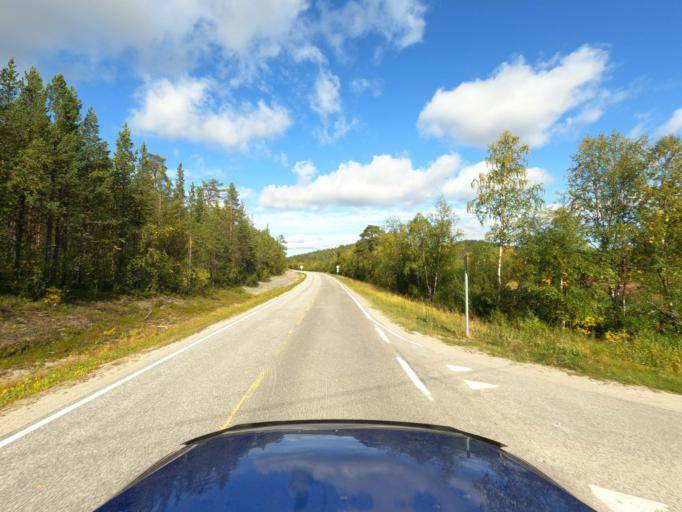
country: NO
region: Finnmark Fylke
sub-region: Karasjok
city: Karasjohka
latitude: 69.4783
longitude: 25.5173
